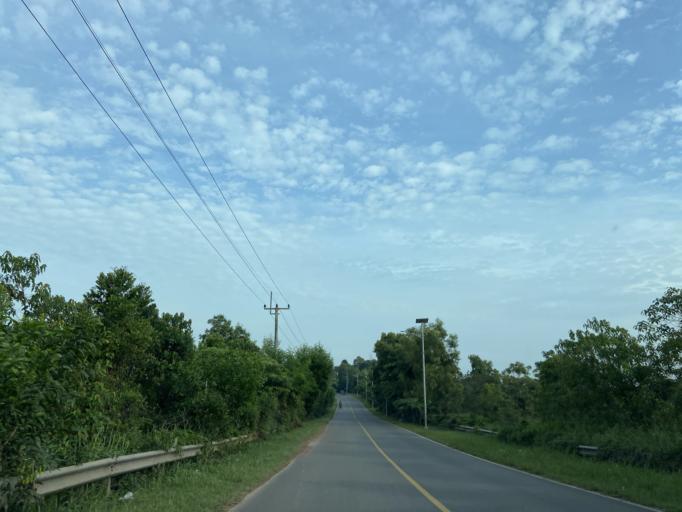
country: ID
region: Riau Islands
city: Tanjungpinang
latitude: 0.9324
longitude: 104.1103
